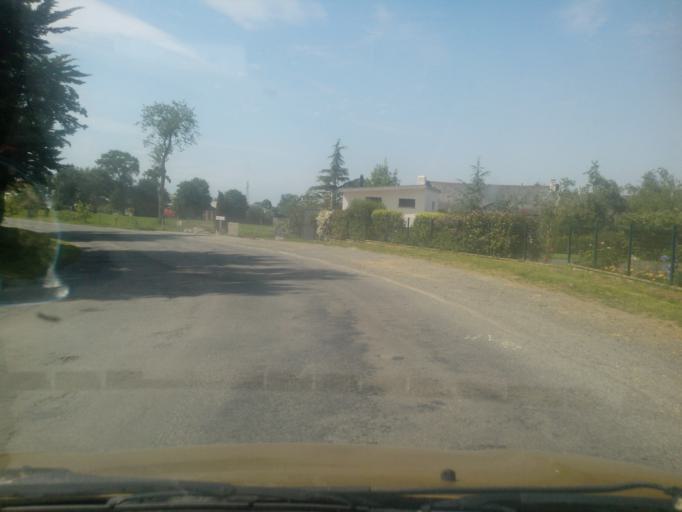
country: FR
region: Brittany
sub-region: Departement d'Ille-et-Vilaine
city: Melesse
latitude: 48.2290
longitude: -1.6999
